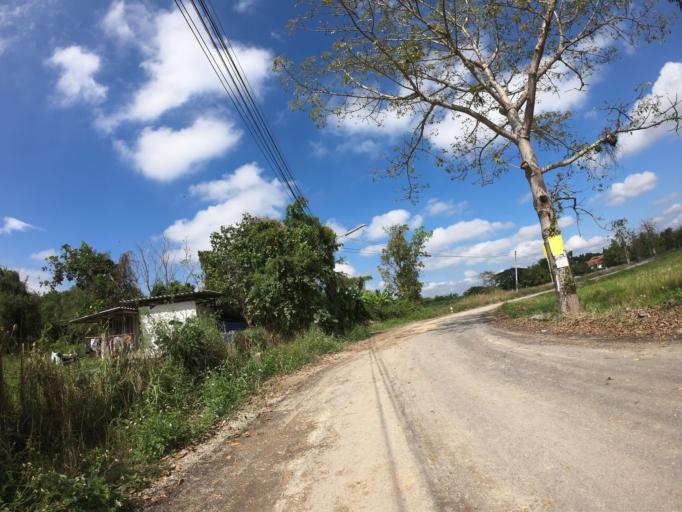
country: TH
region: Chiang Mai
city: San Sai
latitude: 18.8231
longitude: 99.0578
